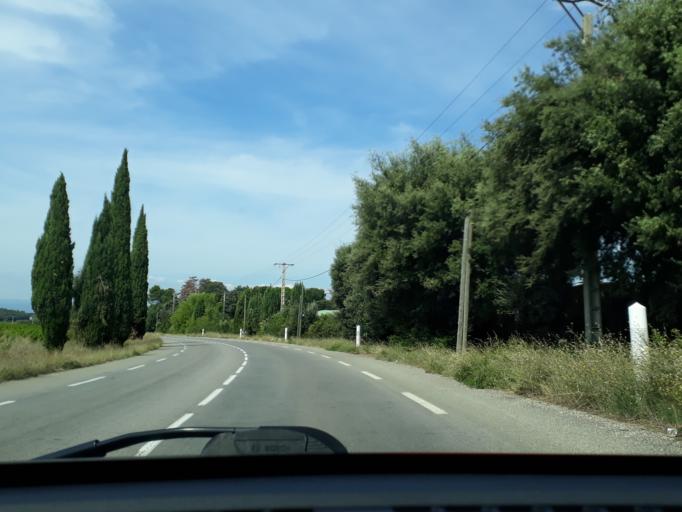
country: FR
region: Rhone-Alpes
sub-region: Departement de la Drome
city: Rochegude
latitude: 44.2618
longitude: 4.8223
